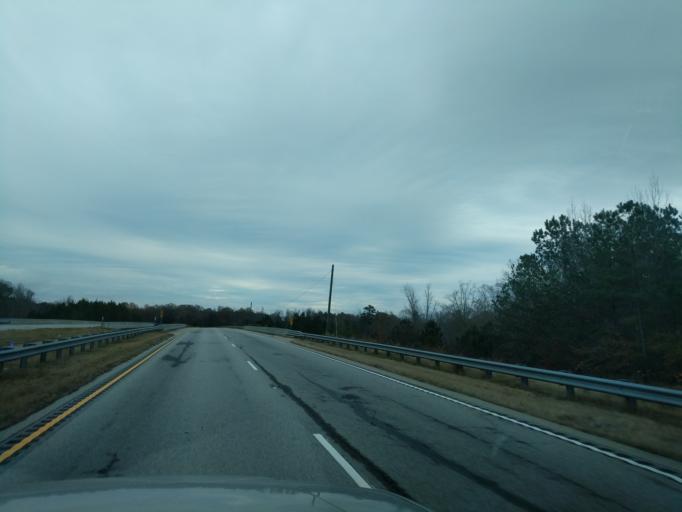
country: US
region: South Carolina
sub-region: Laurens County
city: Clinton
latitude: 34.3479
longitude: -81.9705
